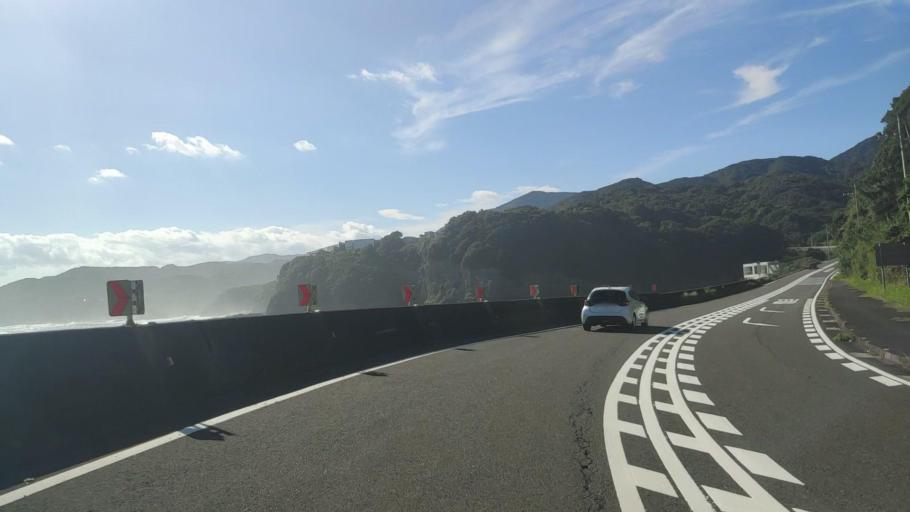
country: JP
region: Wakayama
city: Tanabe
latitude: 33.5039
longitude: 135.6403
